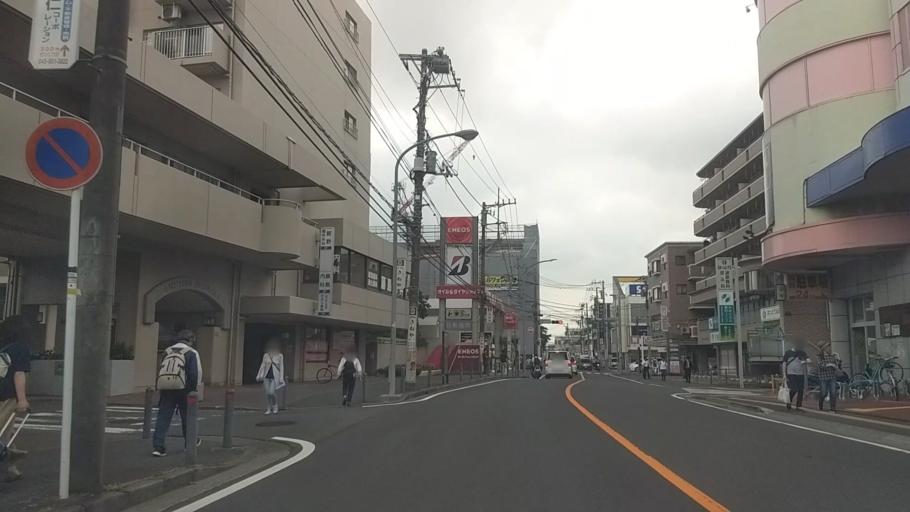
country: JP
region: Kanagawa
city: Fujisawa
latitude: 35.3987
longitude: 139.5365
